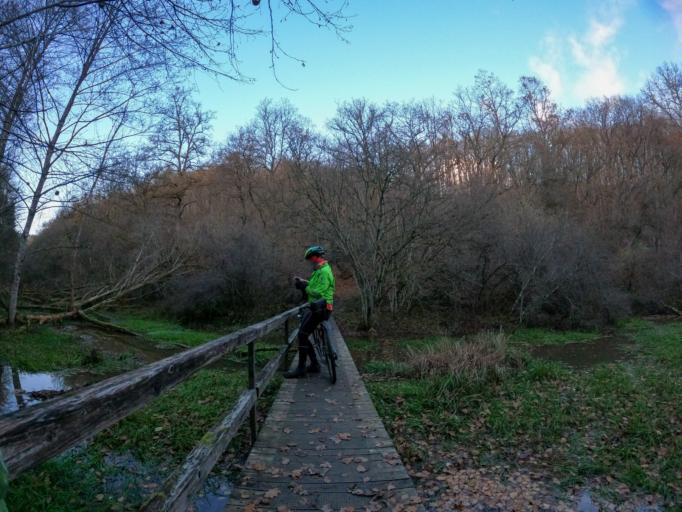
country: LU
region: Diekirch
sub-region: Canton de Wiltz
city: Bavigne
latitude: 49.9153
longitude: 5.8575
